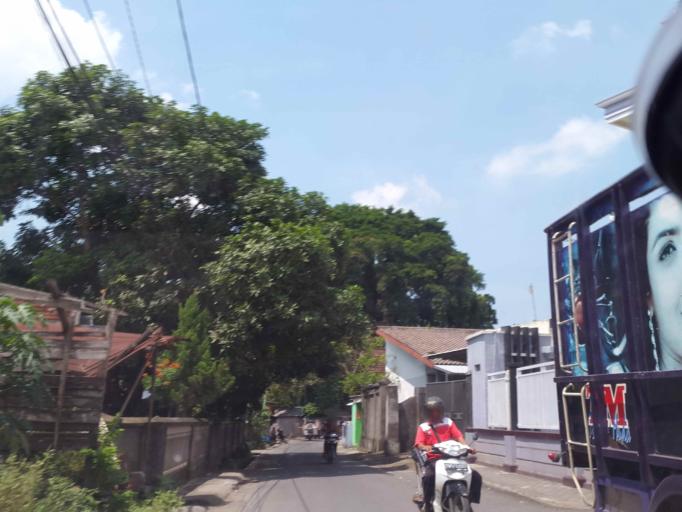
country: ID
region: West Nusa Tenggara
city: Mambalan
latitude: -8.5480
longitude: 116.1121
